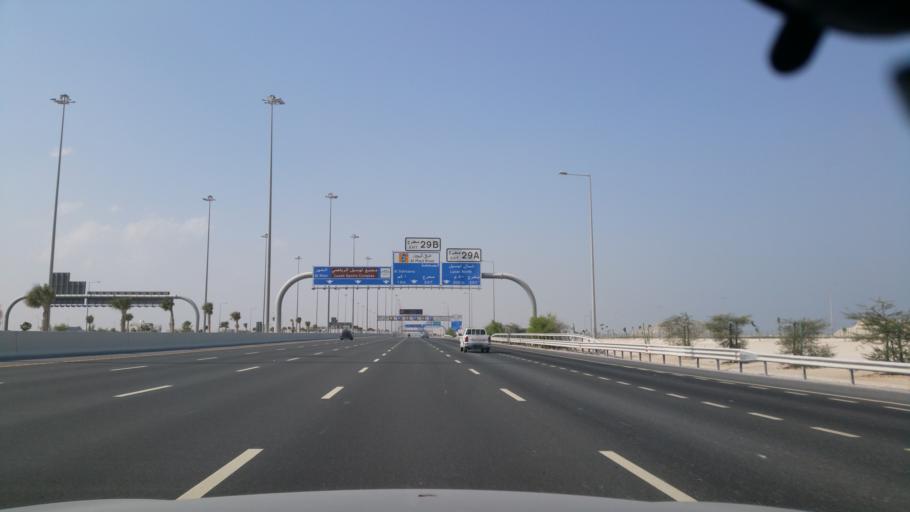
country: QA
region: Baladiyat Umm Salal
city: Umm Salal Muhammad
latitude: 25.4391
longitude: 51.4825
